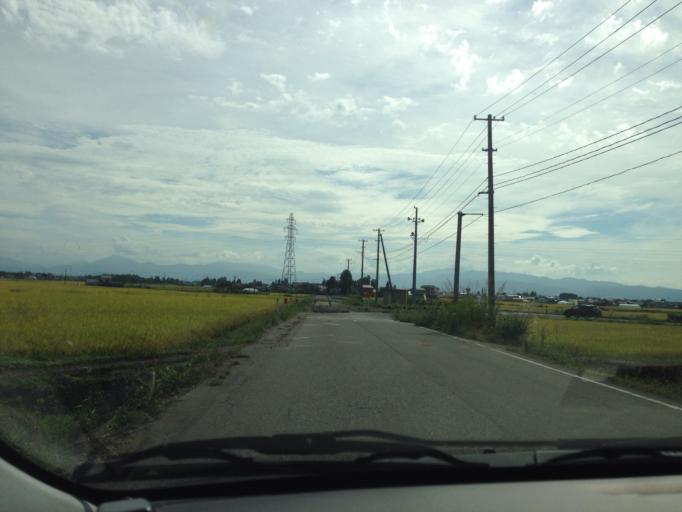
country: JP
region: Fukushima
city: Kitakata
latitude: 37.5969
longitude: 139.9129
